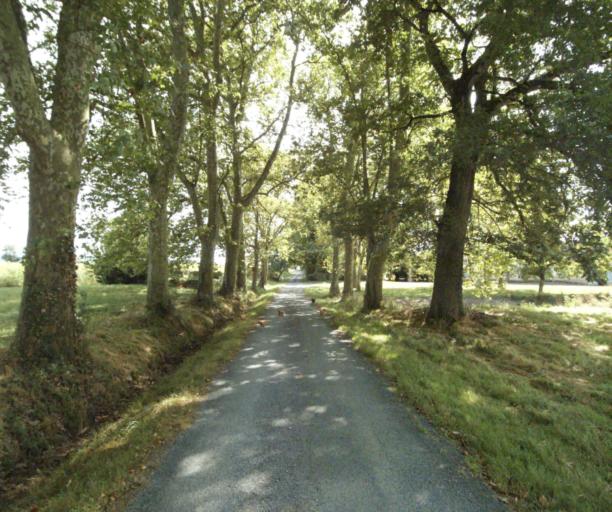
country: FR
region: Midi-Pyrenees
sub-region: Departement du Tarn
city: Soual
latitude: 43.5158
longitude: 2.0740
